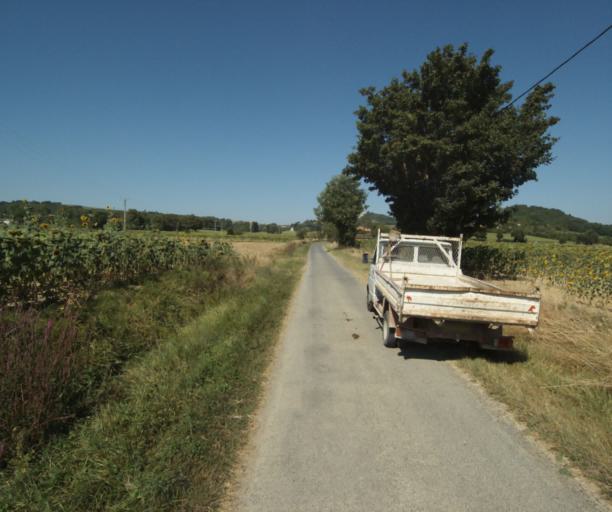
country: FR
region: Midi-Pyrenees
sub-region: Departement de la Haute-Garonne
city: Revel
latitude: 43.5074
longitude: 1.9547
